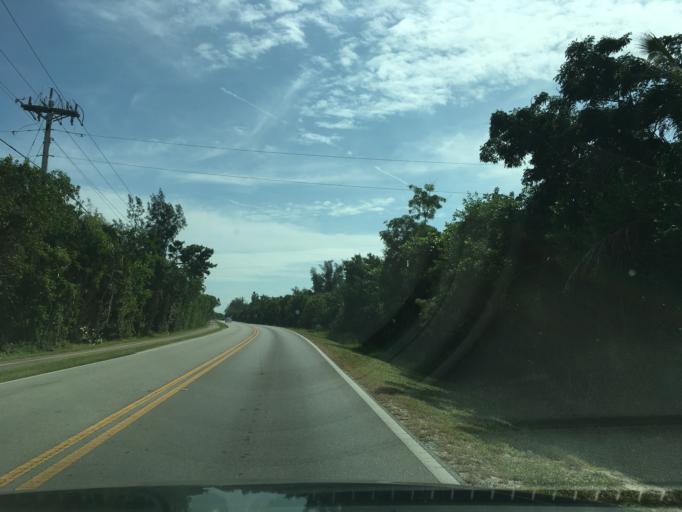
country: US
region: Florida
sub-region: Lee County
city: Saint James City
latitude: 26.4766
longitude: -82.1748
